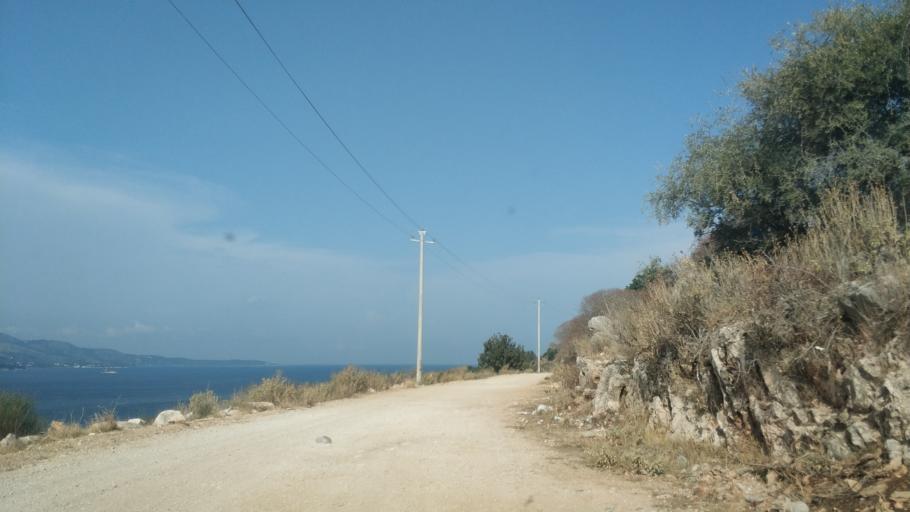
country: AL
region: Vlore
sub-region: Rrethi i Sarandes
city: Xarre
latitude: 39.7914
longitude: 20.0066
